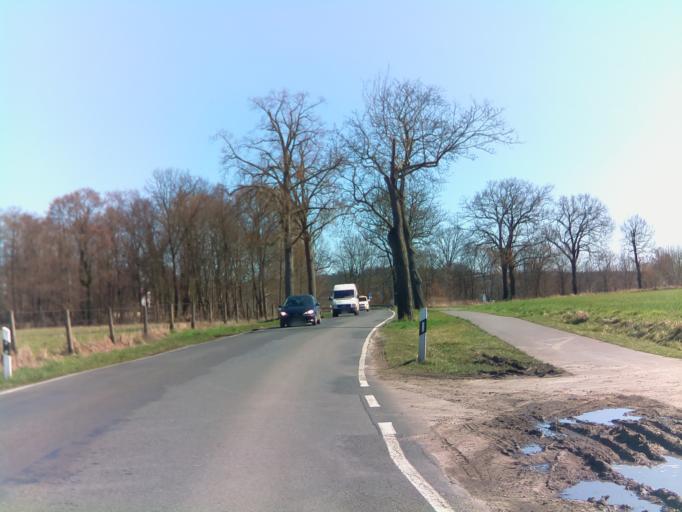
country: DE
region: Brandenburg
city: Werder
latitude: 52.4316
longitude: 12.9602
